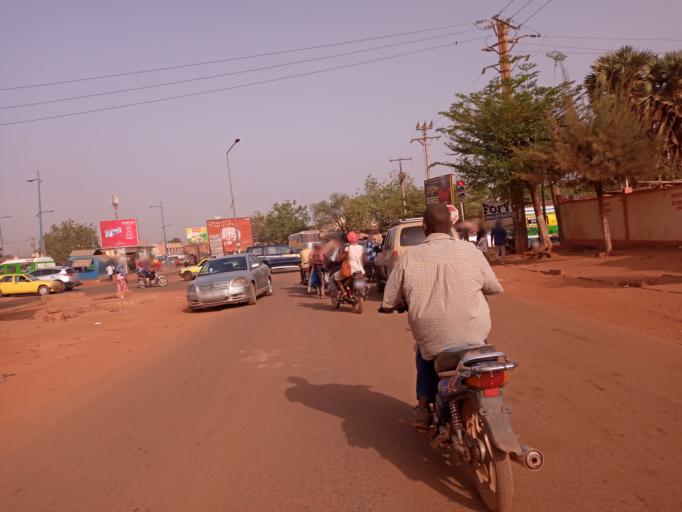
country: ML
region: Bamako
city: Bamako
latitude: 12.6010
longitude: -7.9645
